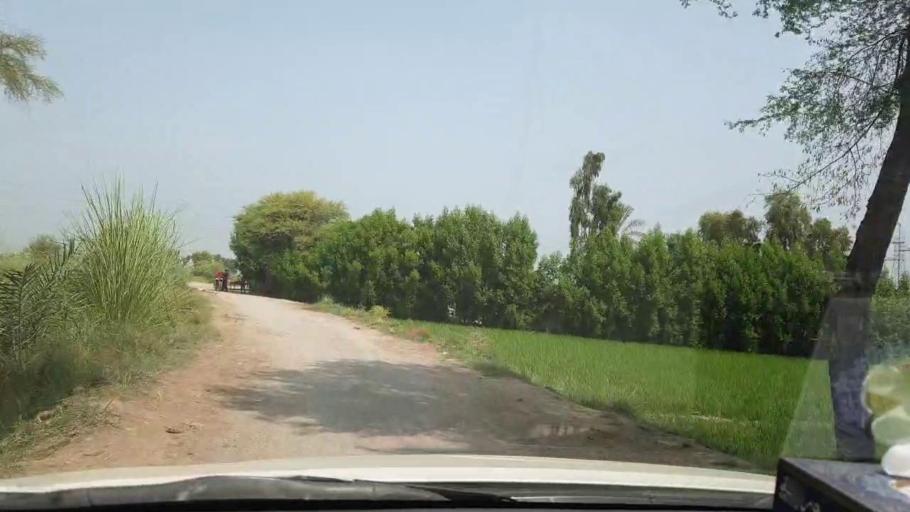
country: PK
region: Sindh
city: Shikarpur
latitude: 27.9880
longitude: 68.6980
